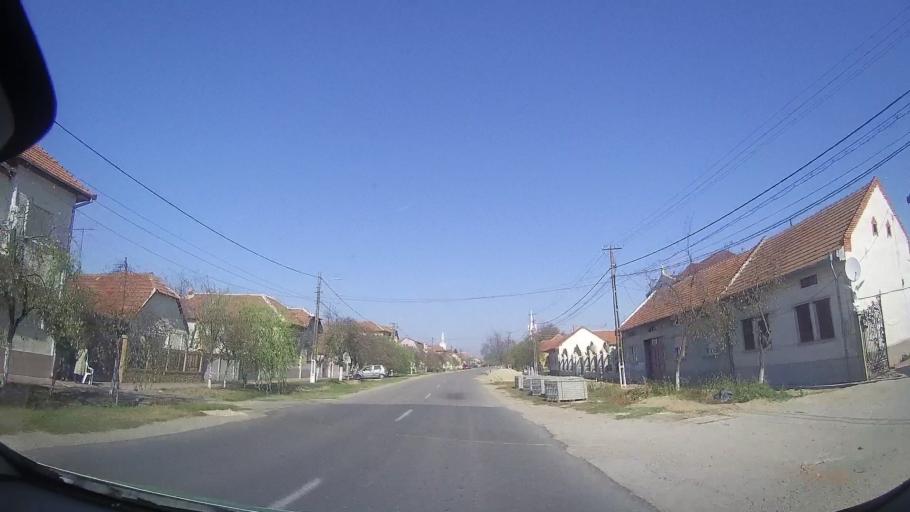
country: RO
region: Timis
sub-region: Comuna Costeiu
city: Costeiu
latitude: 45.7396
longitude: 21.8490
